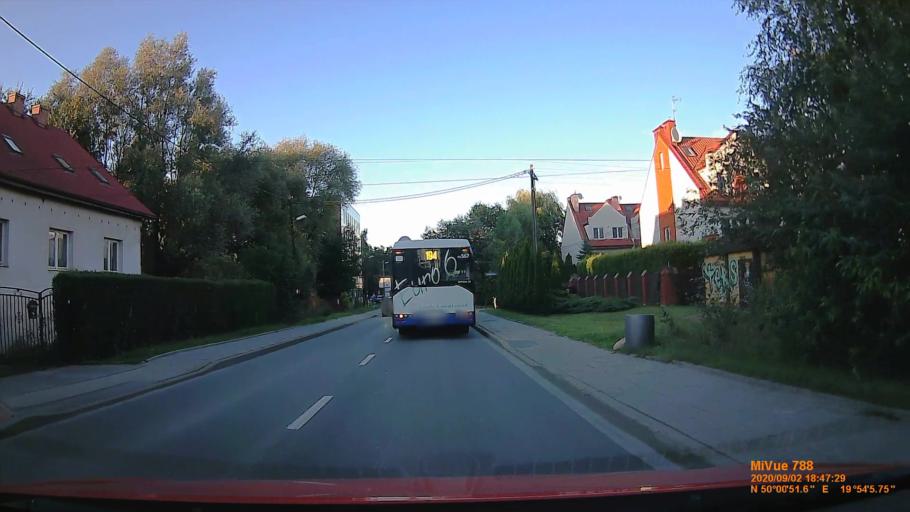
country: PL
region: Lesser Poland Voivodeship
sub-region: Krakow
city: Sidzina
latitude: 50.0145
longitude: 19.9017
